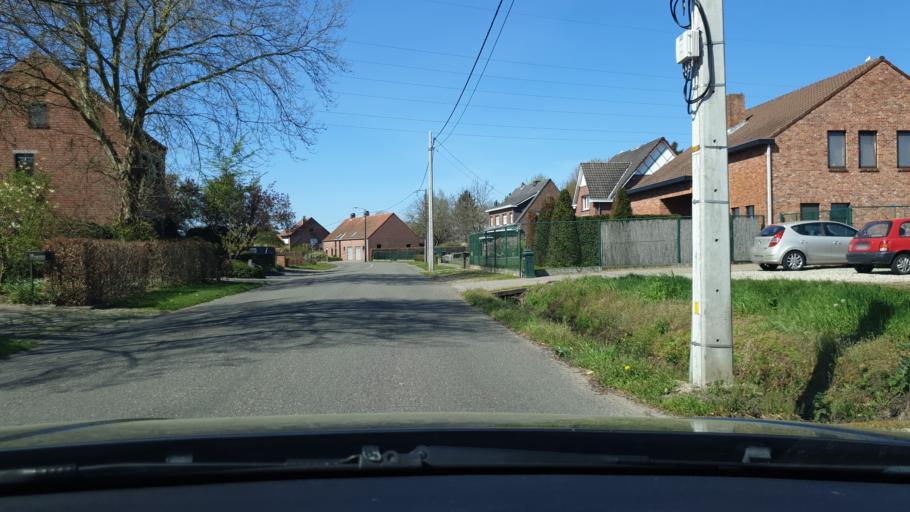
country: BE
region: Flanders
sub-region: Provincie Antwerpen
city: Geel
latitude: 51.1731
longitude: 4.9520
